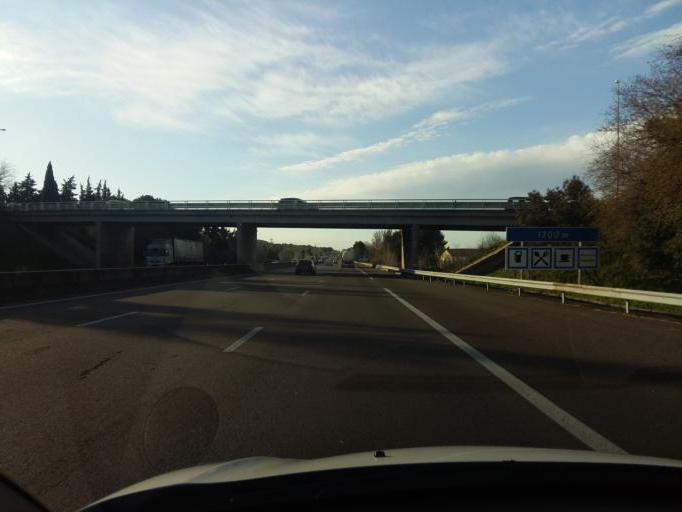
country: FR
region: Provence-Alpes-Cote d'Azur
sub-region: Departement du Vaucluse
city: Morieres-les-Avignon
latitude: 43.9342
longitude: 4.9108
